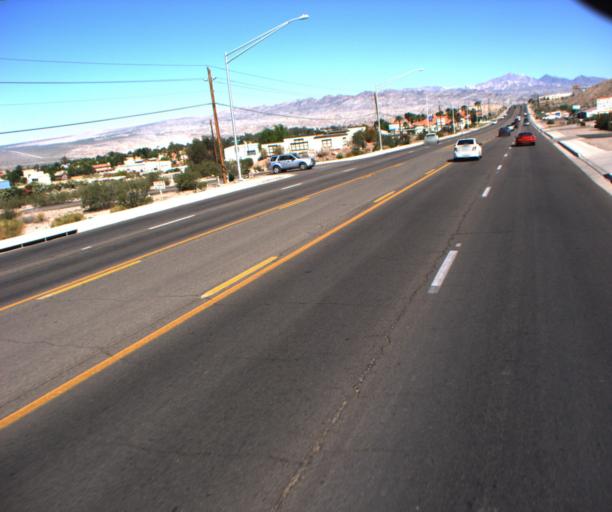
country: US
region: Arizona
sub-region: Mohave County
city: Bullhead City
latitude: 35.0730
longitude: -114.5910
